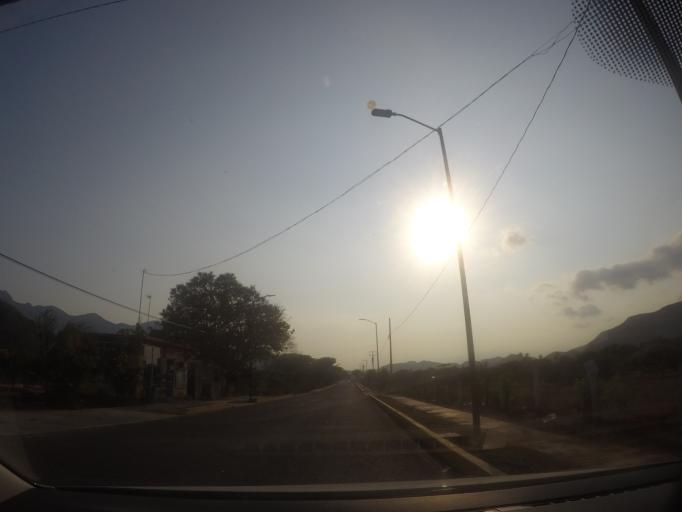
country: MX
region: Oaxaca
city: San Jeronimo Ixtepec
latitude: 16.5823
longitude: -95.1948
